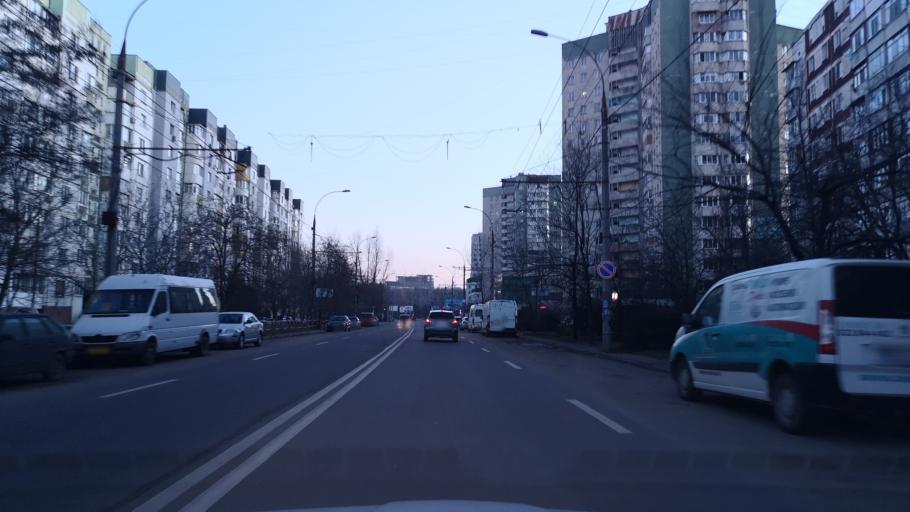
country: MD
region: Chisinau
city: Stauceni
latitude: 47.0564
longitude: 28.8486
